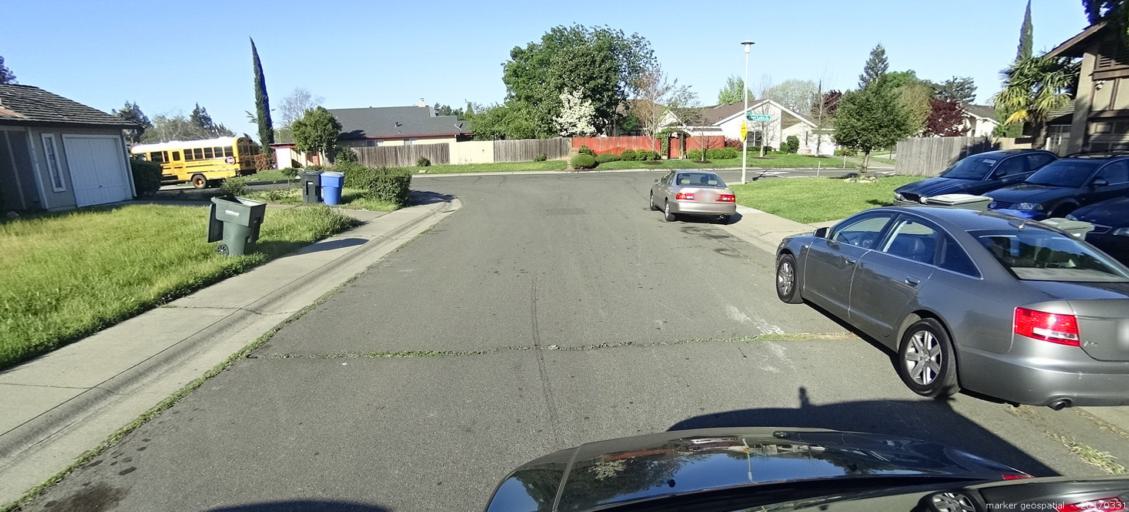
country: US
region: California
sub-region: Sacramento County
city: Parkway
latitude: 38.4661
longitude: -121.4565
